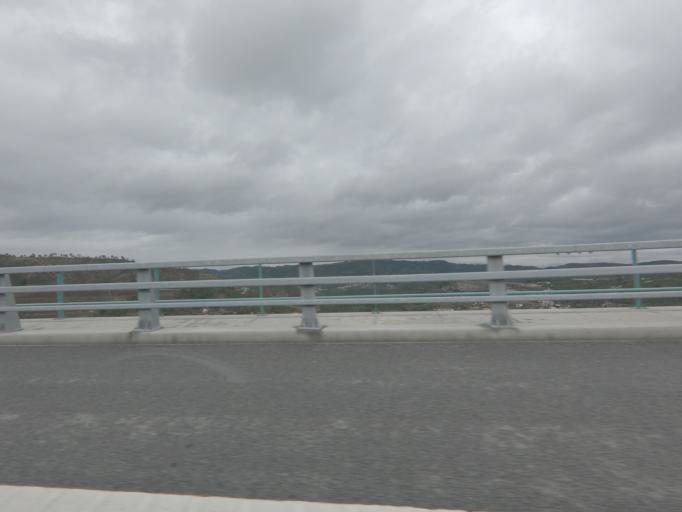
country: PT
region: Porto
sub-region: Amarante
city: Amarante
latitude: 41.2521
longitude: -7.9837
